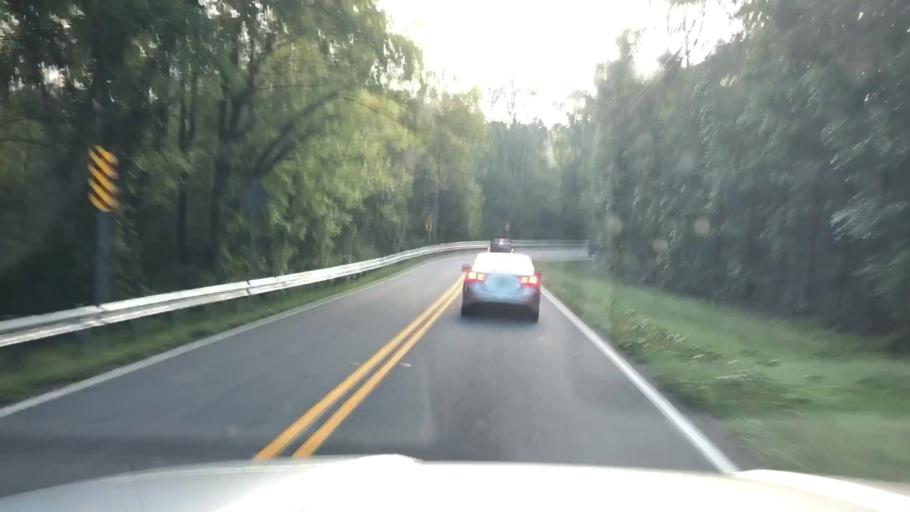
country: US
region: Georgia
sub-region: Bartow County
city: Emerson
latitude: 34.0818
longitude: -84.7602
